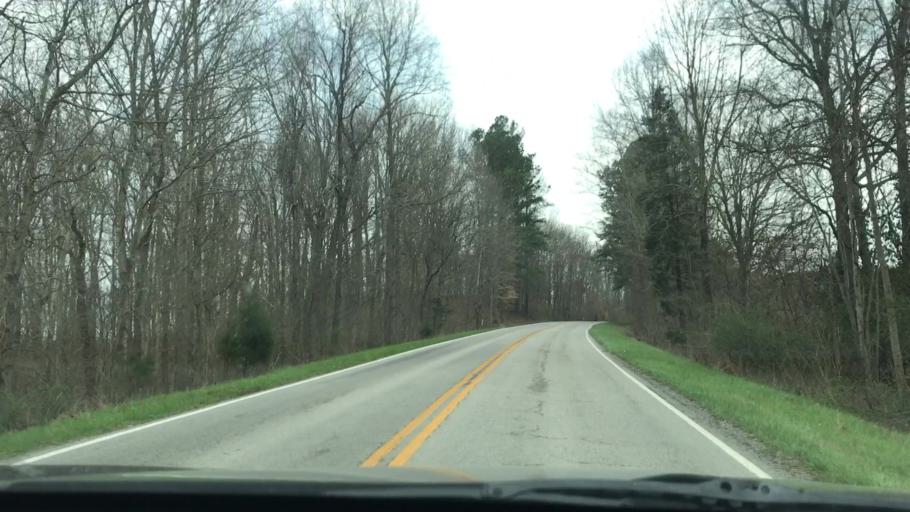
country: US
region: Kentucky
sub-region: Hart County
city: Munfordville
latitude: 37.3122
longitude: -85.7620
